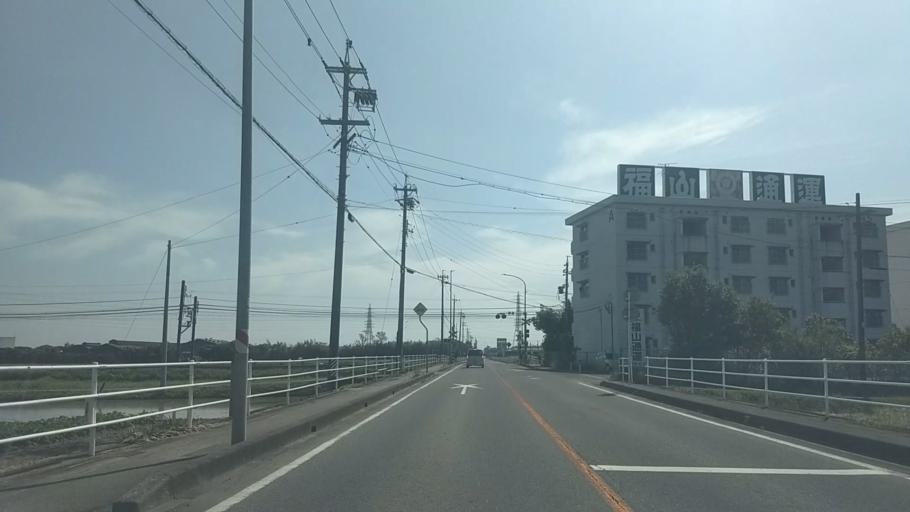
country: JP
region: Aichi
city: Anjo
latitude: 34.9756
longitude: 137.1123
